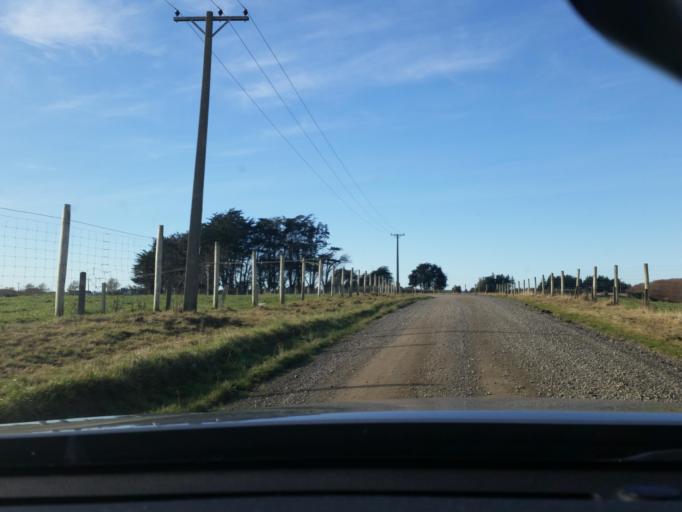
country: NZ
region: Southland
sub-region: Southland District
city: Riverton
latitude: -46.3017
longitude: 168.0350
